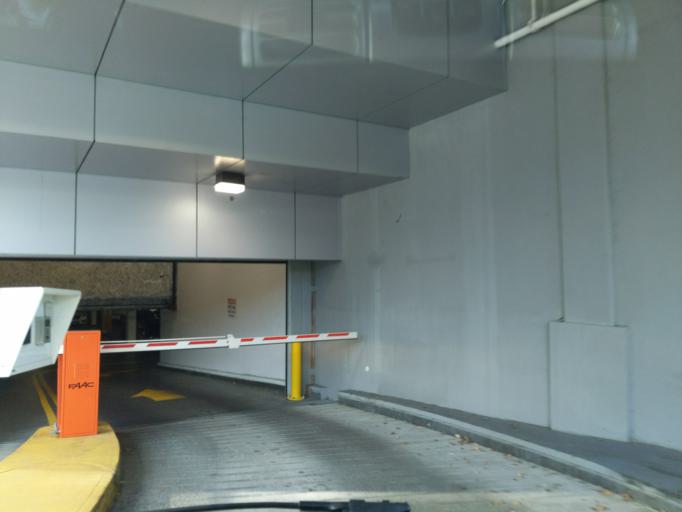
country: CA
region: British Columbia
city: Burnaby
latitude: 49.2533
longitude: -123.0109
